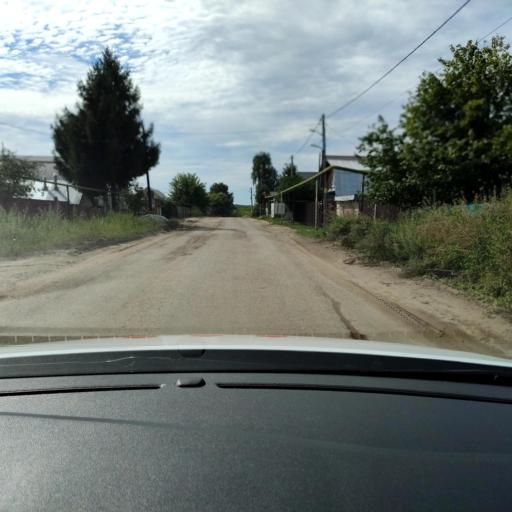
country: RU
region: Tatarstan
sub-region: Gorod Kazan'
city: Kazan
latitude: 55.7159
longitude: 49.0905
